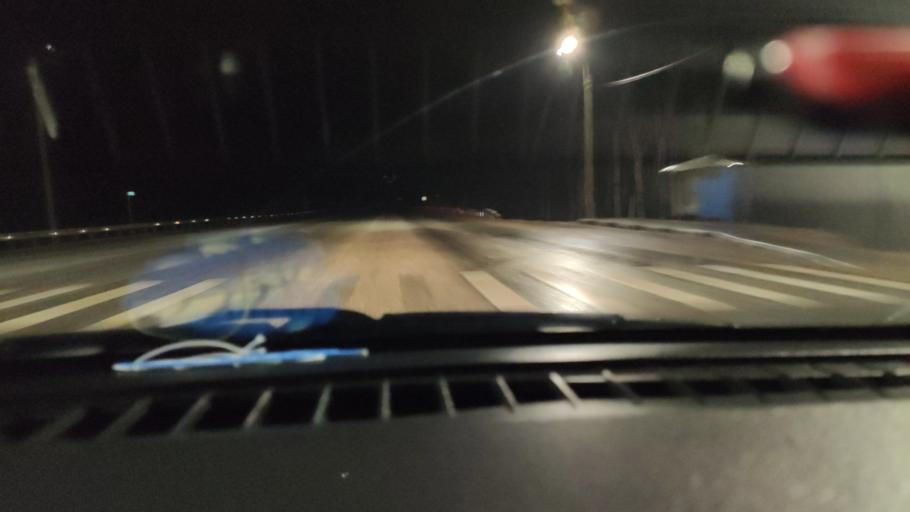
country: RU
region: Udmurtiya
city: Khokhryaki
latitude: 56.9379
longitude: 53.5686
